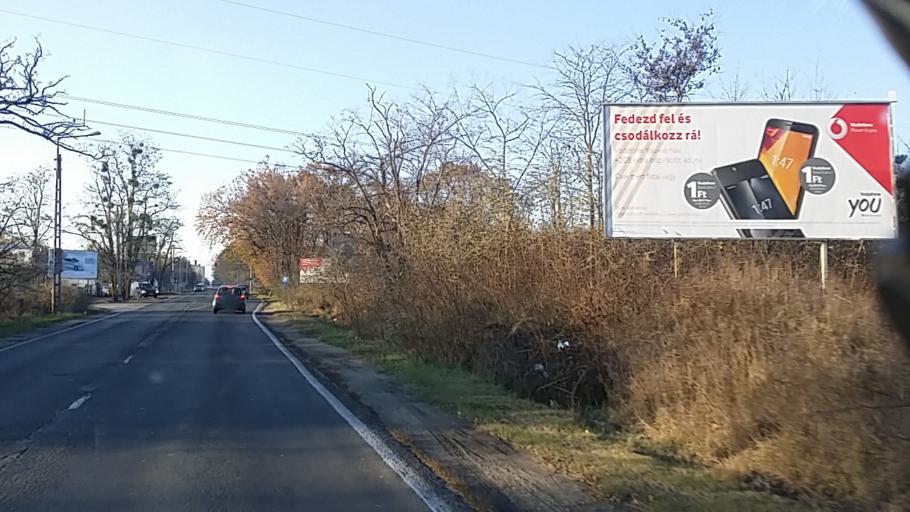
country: HU
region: Budapest
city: Budapest XVI. keruelet
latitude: 47.5406
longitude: 19.1541
